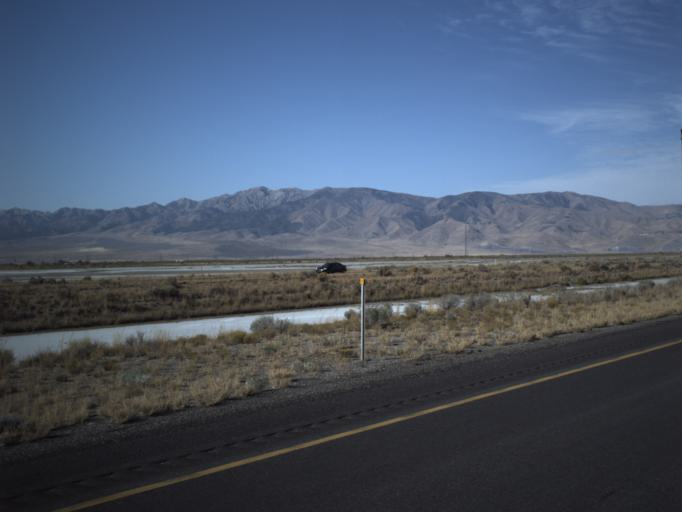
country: US
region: Utah
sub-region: Tooele County
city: Grantsville
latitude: 40.6812
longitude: -112.4235
